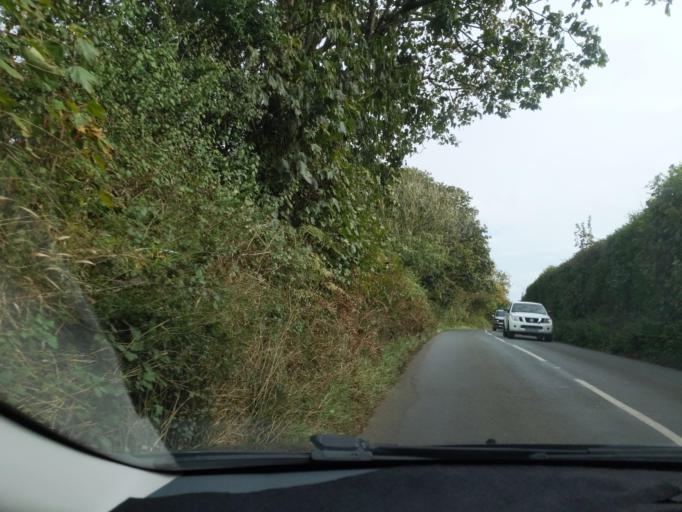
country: GB
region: England
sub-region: Cornwall
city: Mevagissey
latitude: 50.2484
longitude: -4.8172
